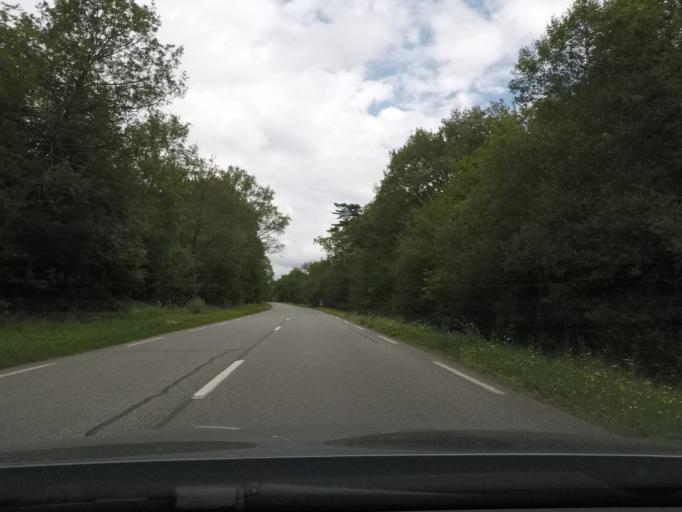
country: FR
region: Auvergne
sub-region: Departement du Puy-de-Dome
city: Randan
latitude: 46.0328
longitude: 3.3587
